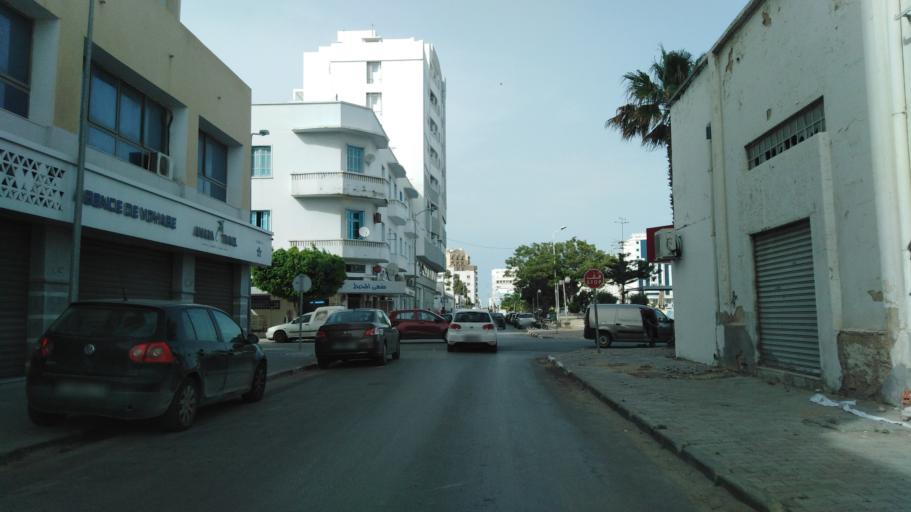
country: TN
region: Safaqis
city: Sfax
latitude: 34.7287
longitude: 10.7606
